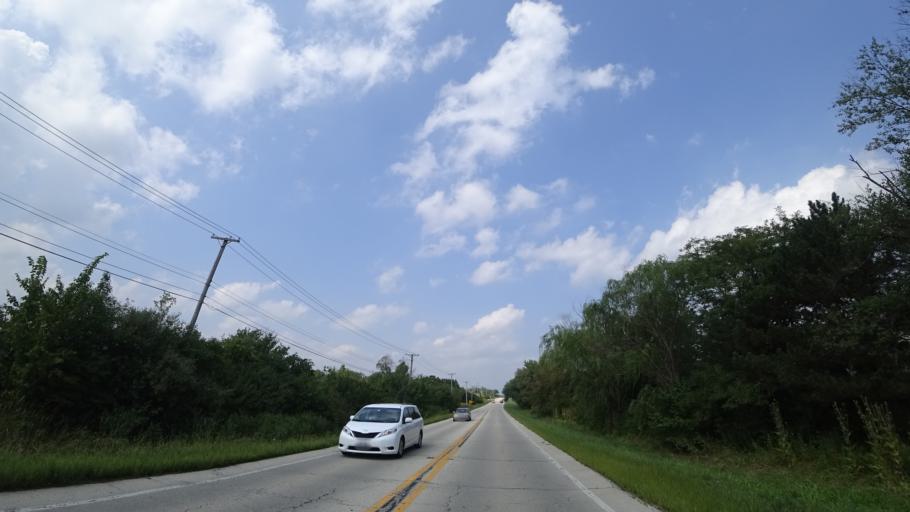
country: US
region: Illinois
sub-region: Will County
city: Goodings Grove
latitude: 41.6386
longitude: -87.8926
